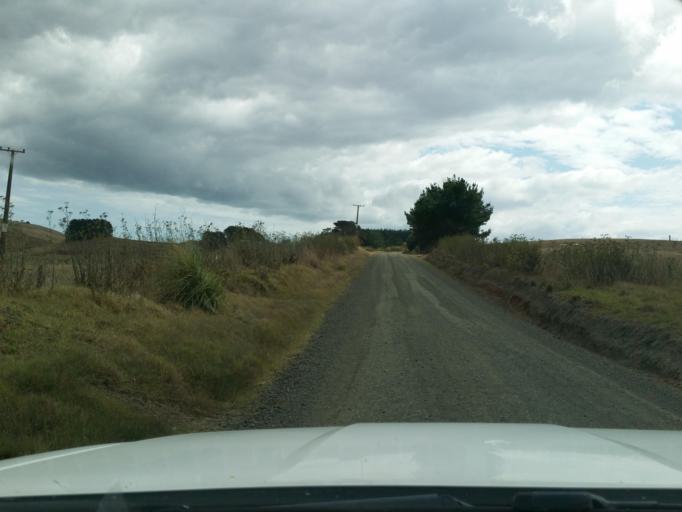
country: NZ
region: Auckland
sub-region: Auckland
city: Wellsford
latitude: -36.3399
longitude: 174.1623
